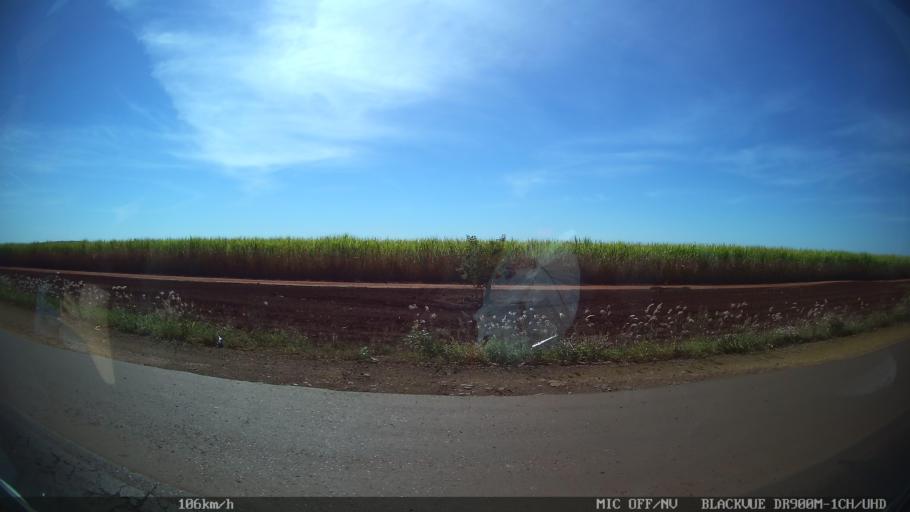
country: BR
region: Sao Paulo
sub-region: Ipua
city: Ipua
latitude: -20.4969
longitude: -47.9684
